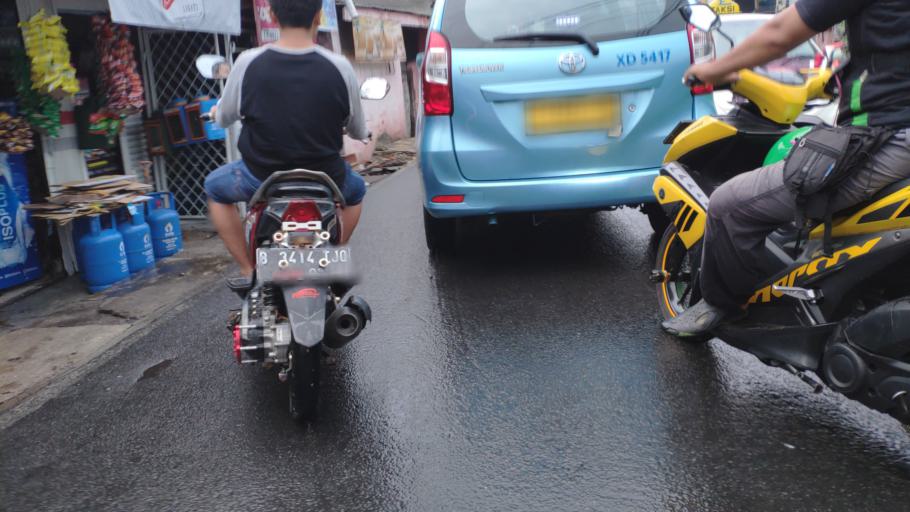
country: ID
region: Jakarta Raya
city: Jakarta
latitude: -6.2036
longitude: 106.8671
